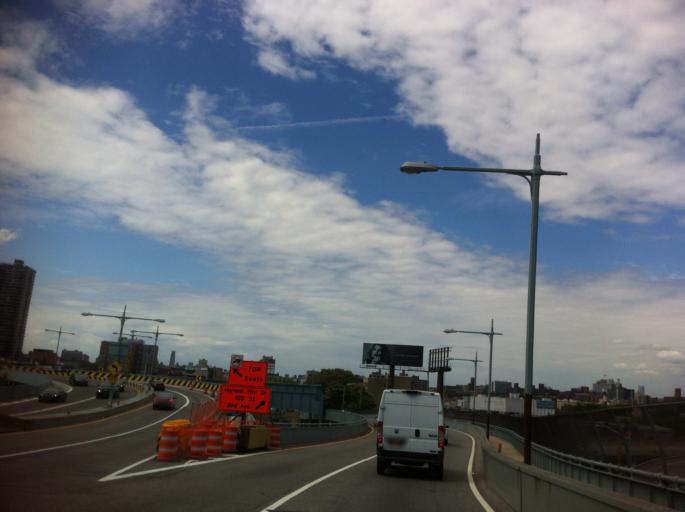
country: US
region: New York
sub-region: New York County
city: Manhattan
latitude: 40.7999
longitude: -73.9268
